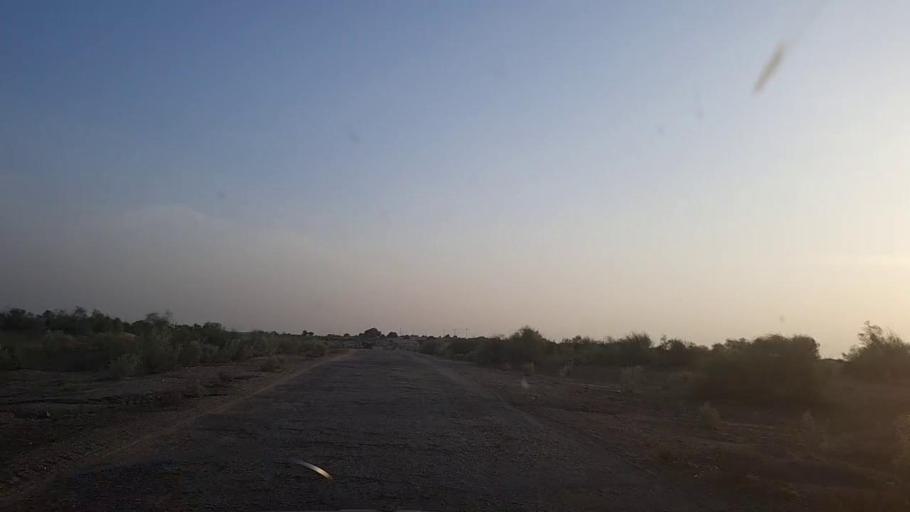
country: PK
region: Sindh
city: Khanpur
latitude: 27.6010
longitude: 69.4304
